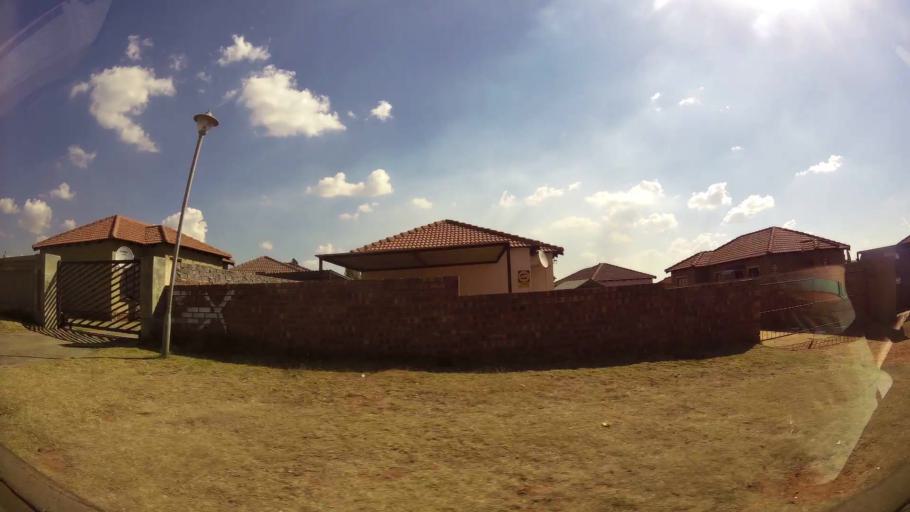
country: ZA
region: Mpumalanga
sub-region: Nkangala District Municipality
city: Witbank
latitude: -25.9467
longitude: 29.2503
